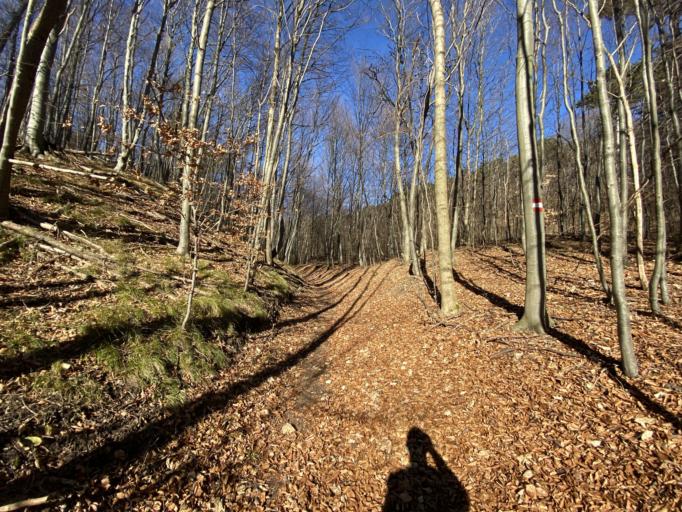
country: AT
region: Lower Austria
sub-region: Politischer Bezirk Baden
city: Heiligenkreuz
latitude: 48.0001
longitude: 16.1469
